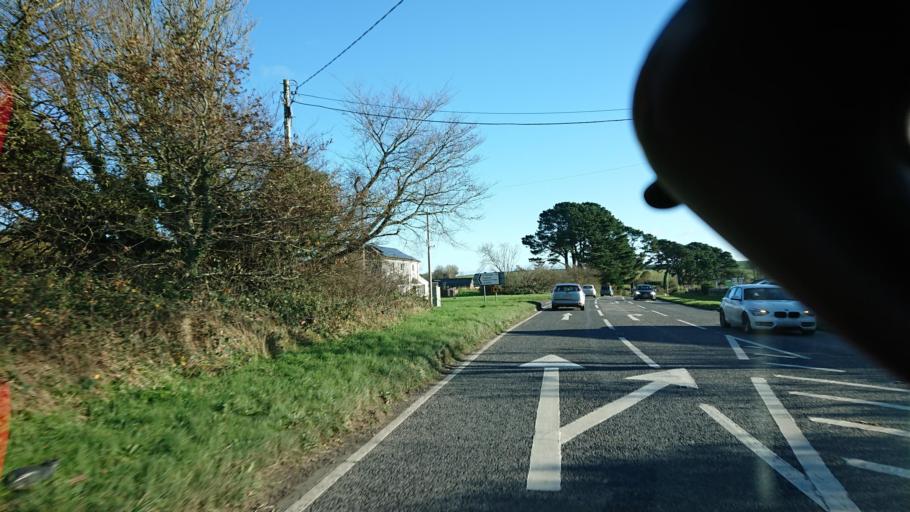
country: GB
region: England
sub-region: Cornwall
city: Pillaton
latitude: 50.4059
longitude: -4.3496
